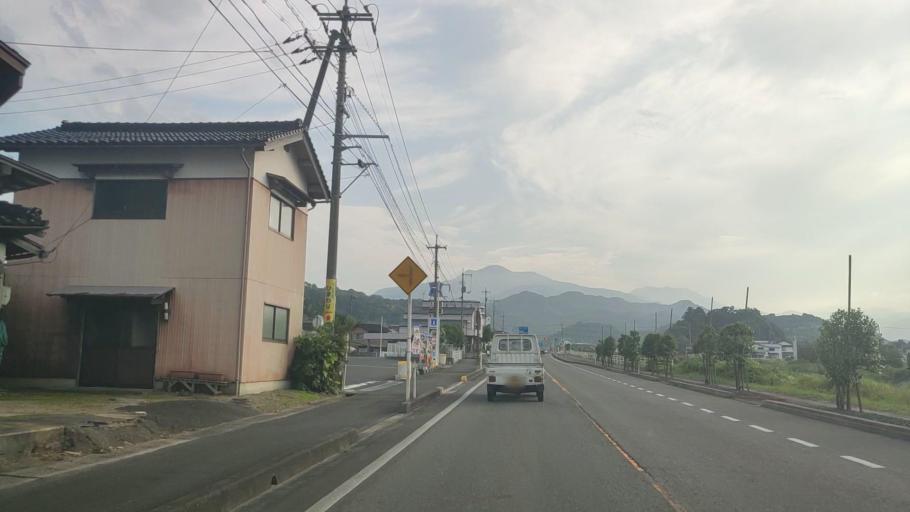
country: JP
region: Tottori
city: Kurayoshi
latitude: 35.3674
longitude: 133.7617
